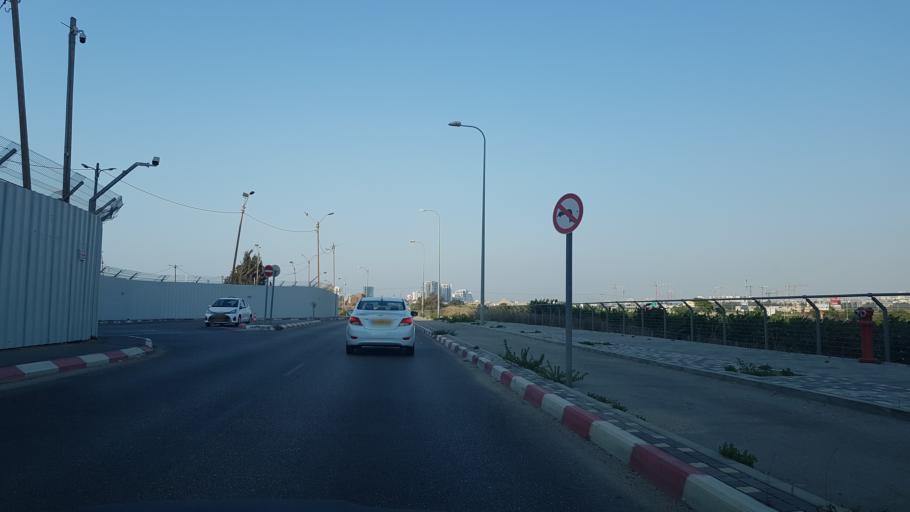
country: IL
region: Tel Aviv
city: Herzliyya
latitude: 32.1439
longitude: 34.8067
